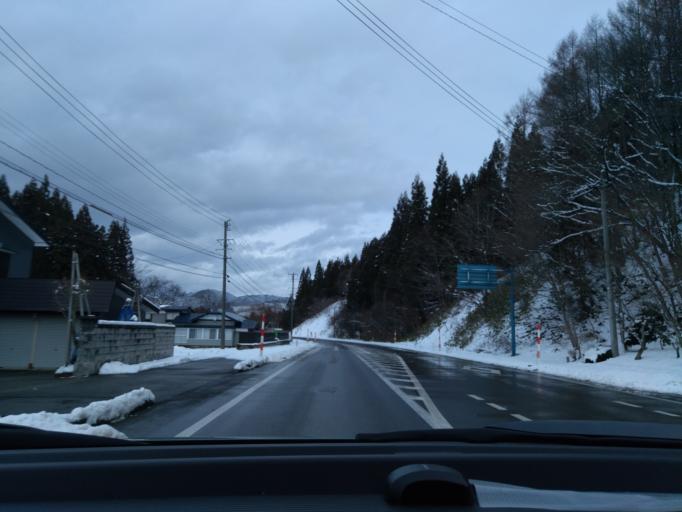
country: JP
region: Akita
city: Kakunodatemachi
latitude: 39.6156
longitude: 140.6306
